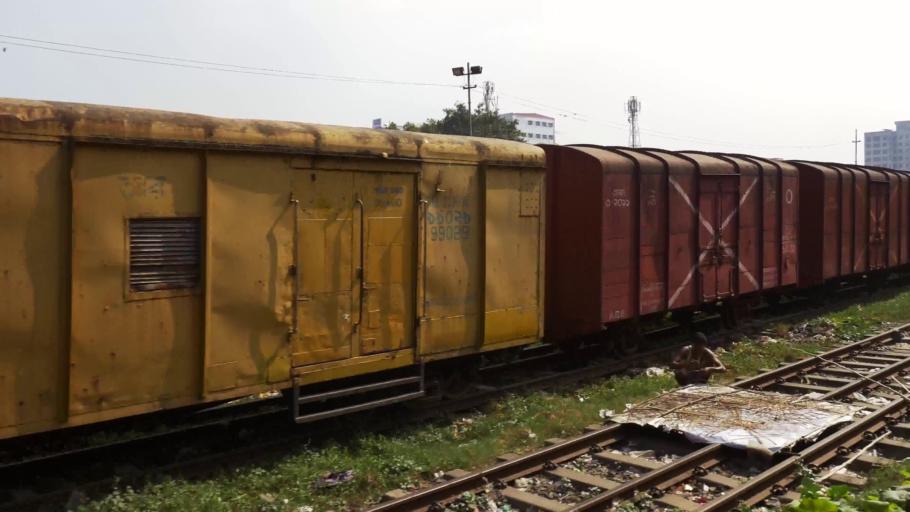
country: BD
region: Dhaka
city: Paltan
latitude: 23.7980
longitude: 90.4011
